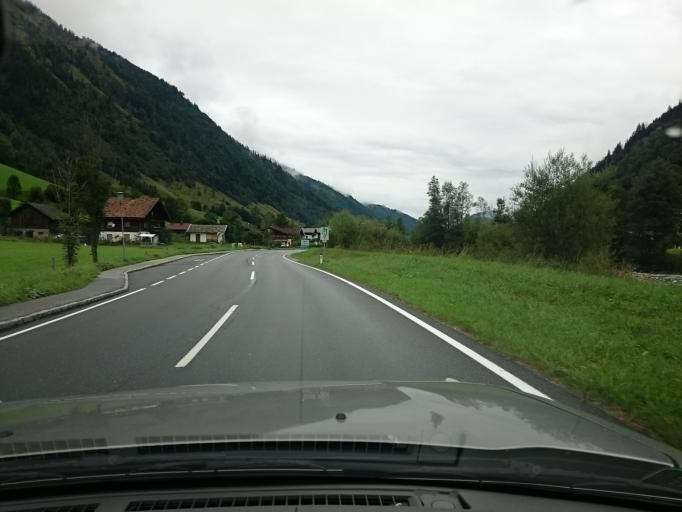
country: AT
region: Salzburg
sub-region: Politischer Bezirk Zell am See
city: Bruck an der Grossglocknerstrasse
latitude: 47.2193
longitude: 12.8276
